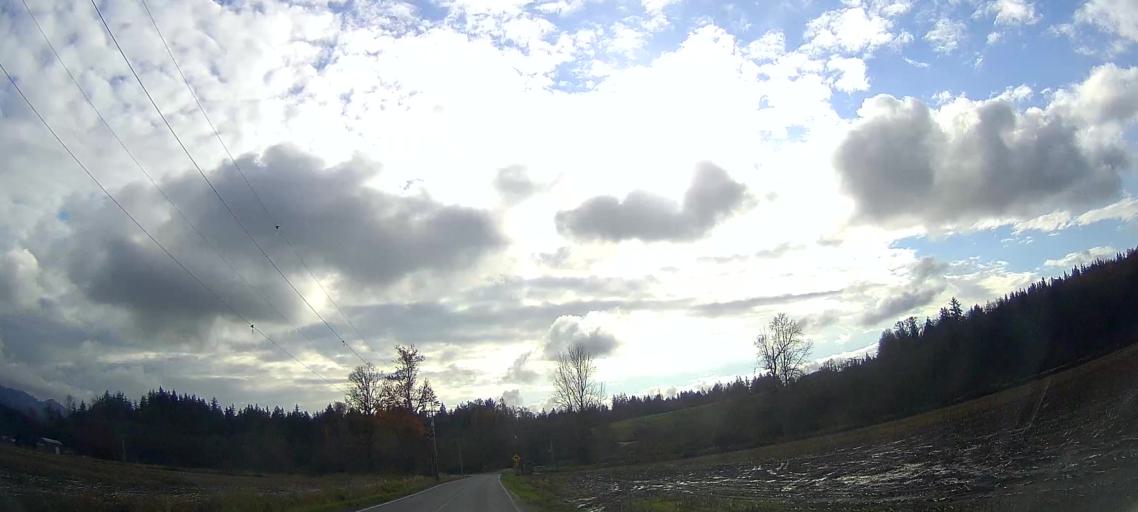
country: US
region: Washington
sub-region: Skagit County
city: Big Lake
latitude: 48.4298
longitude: -122.2204
